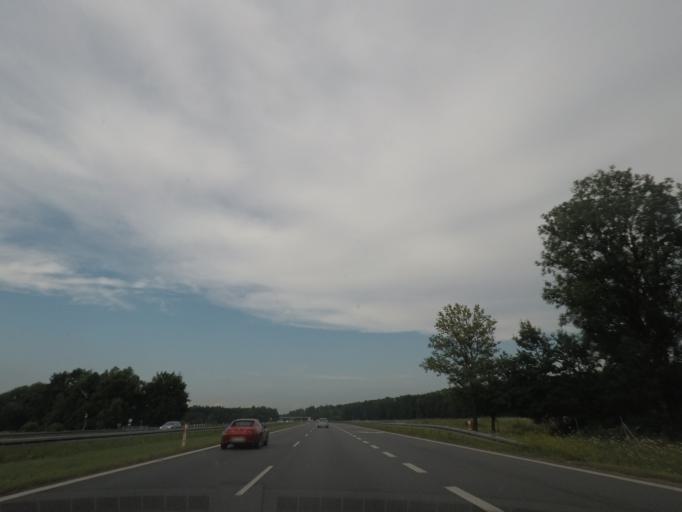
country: PL
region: Lesser Poland Voivodeship
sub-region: Powiat chrzanowski
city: Libiaz
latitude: 50.1480
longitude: 19.3036
